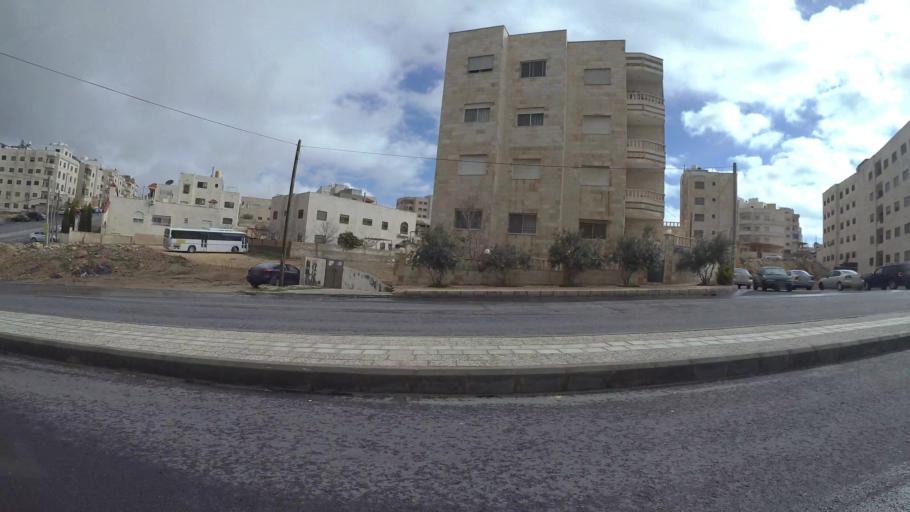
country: JO
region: Amman
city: Al Jubayhah
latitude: 32.0626
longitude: 35.8899
